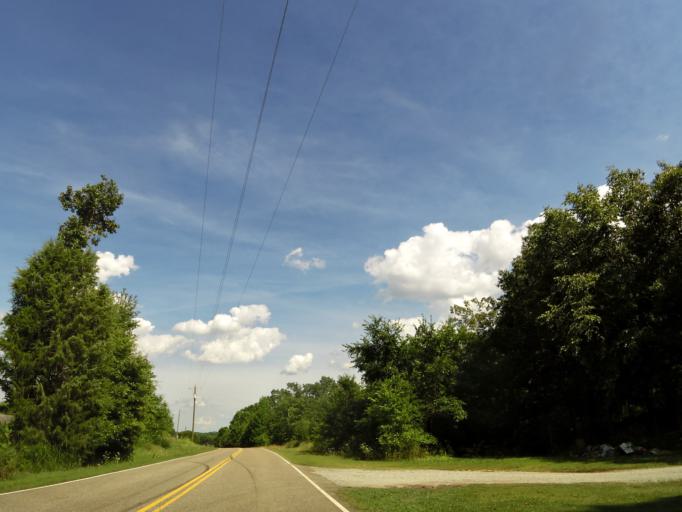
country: US
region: Tennessee
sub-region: Gibson County
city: Milan
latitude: 35.9763
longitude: -88.7209
